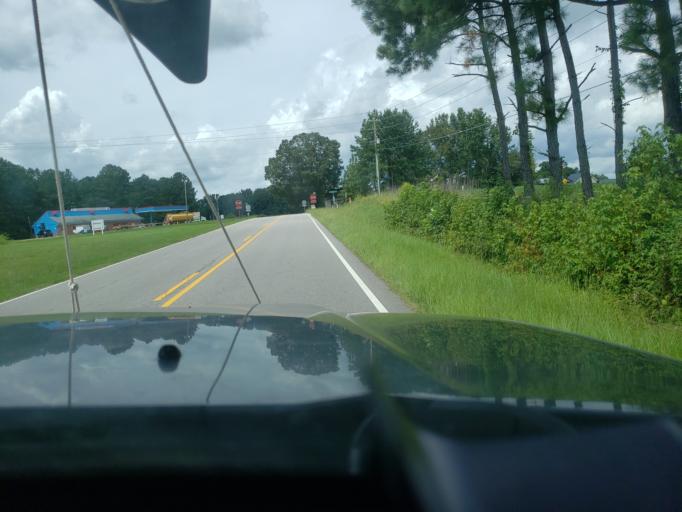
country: US
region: North Carolina
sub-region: Wake County
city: Rolesville
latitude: 35.8918
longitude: -78.4284
